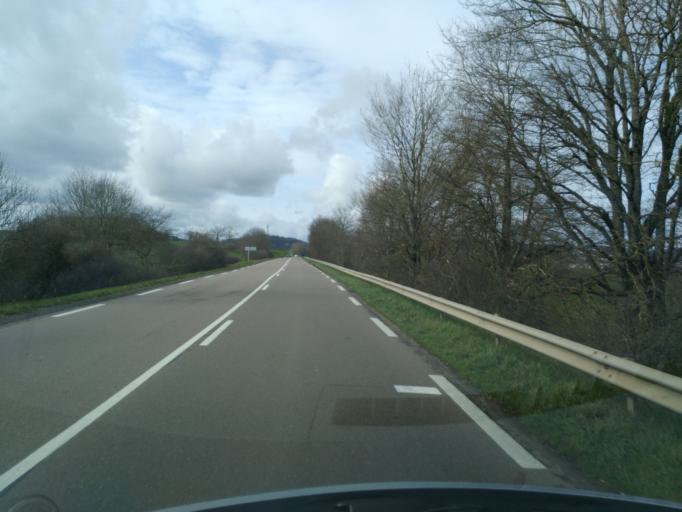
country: FR
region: Bourgogne
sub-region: Departement de Saone-et-Loire
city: Torcy
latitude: 46.7736
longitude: 4.4270
